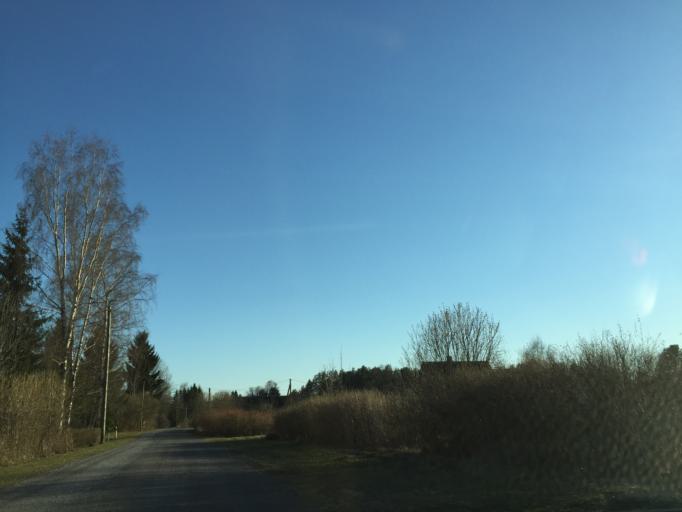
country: EE
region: Ida-Virumaa
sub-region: Sillamaee linn
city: Sillamae
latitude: 59.0859
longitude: 27.7809
